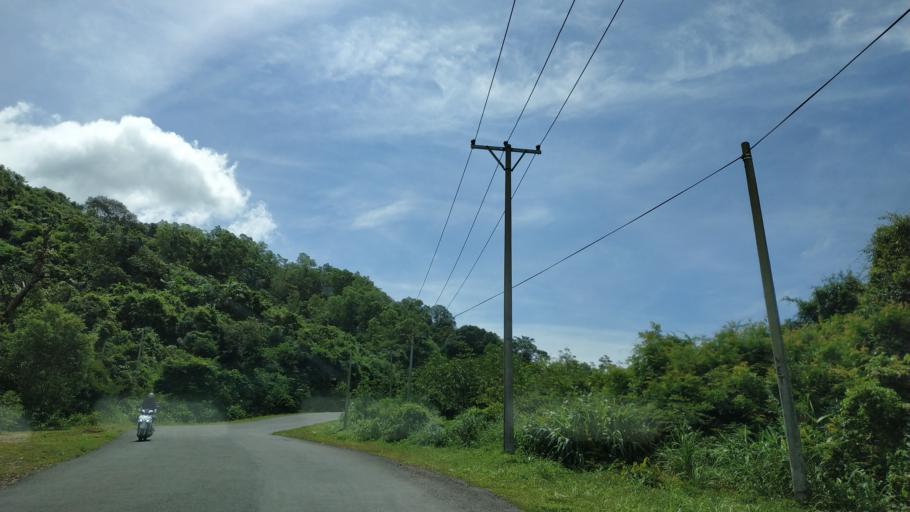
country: MM
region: Tanintharyi
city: Dawei
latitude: 14.1407
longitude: 98.1141
